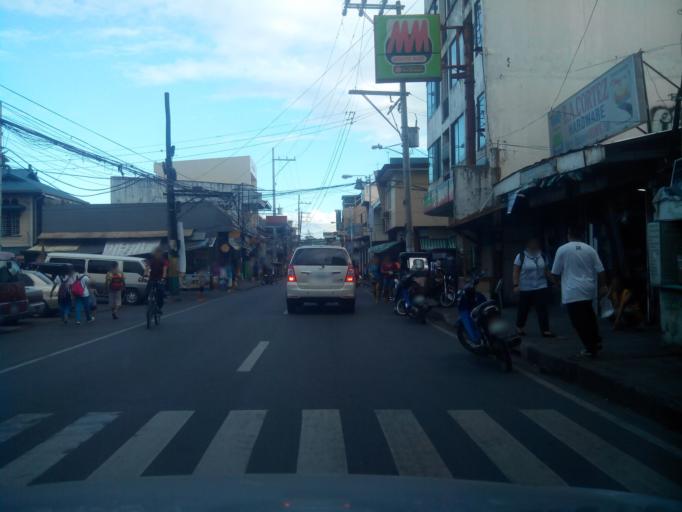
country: PH
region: Calabarzon
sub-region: Province of Rizal
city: Taytay
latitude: 14.5675
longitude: 121.1305
